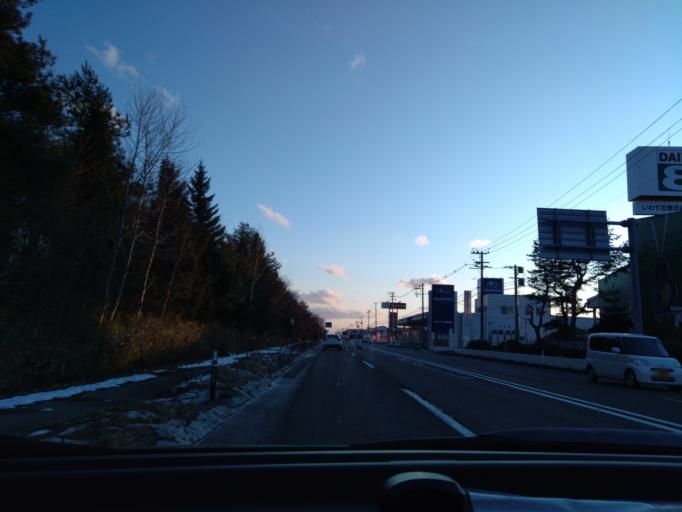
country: JP
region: Iwate
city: Hanamaki
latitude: 39.4350
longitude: 141.1331
